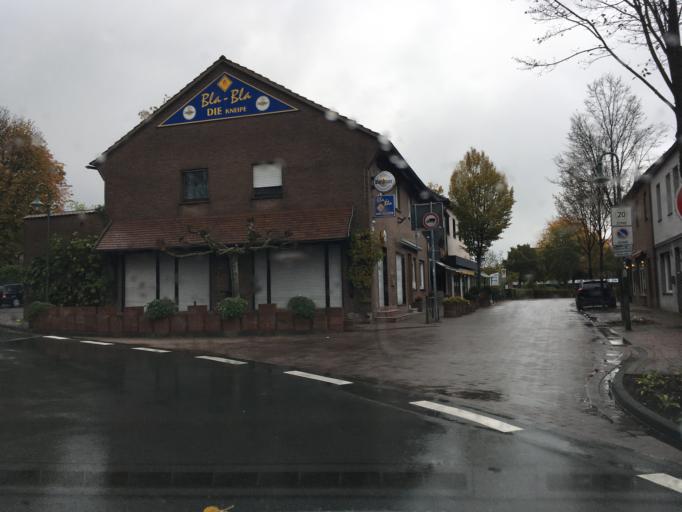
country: DE
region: North Rhine-Westphalia
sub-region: Regierungsbezirk Munster
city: Klein Reken
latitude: 51.8320
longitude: 7.0404
